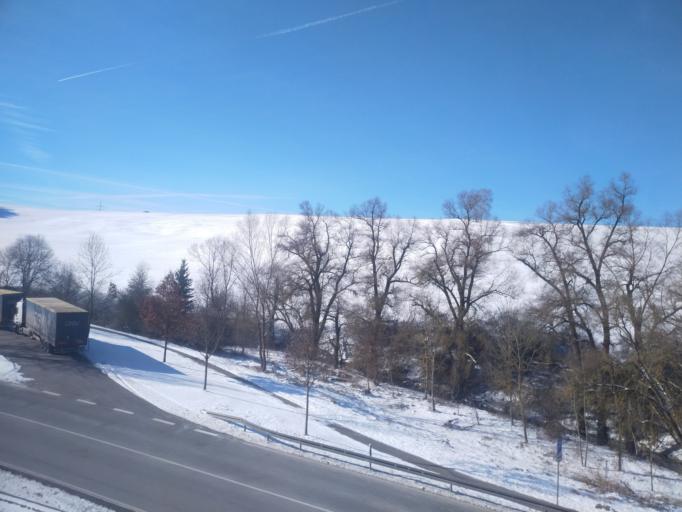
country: DE
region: Baden-Wuerttemberg
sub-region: Freiburg Region
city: Aldingen
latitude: 48.1079
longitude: 8.6965
